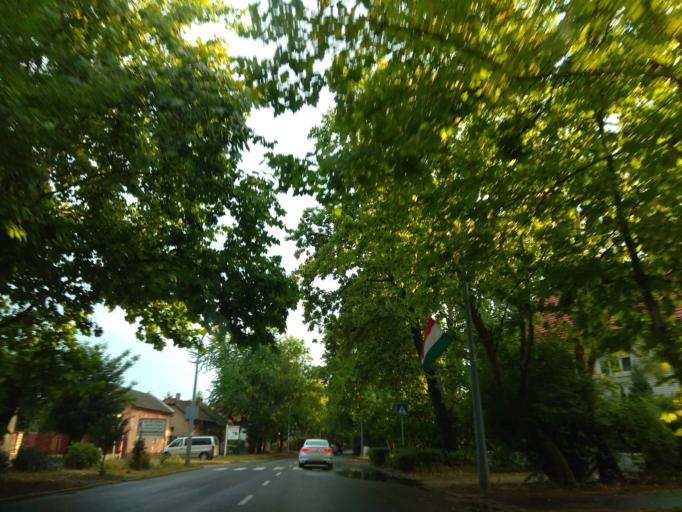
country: HU
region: Borsod-Abauj-Zemplen
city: Miskolc
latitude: 48.0899
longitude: 20.7946
